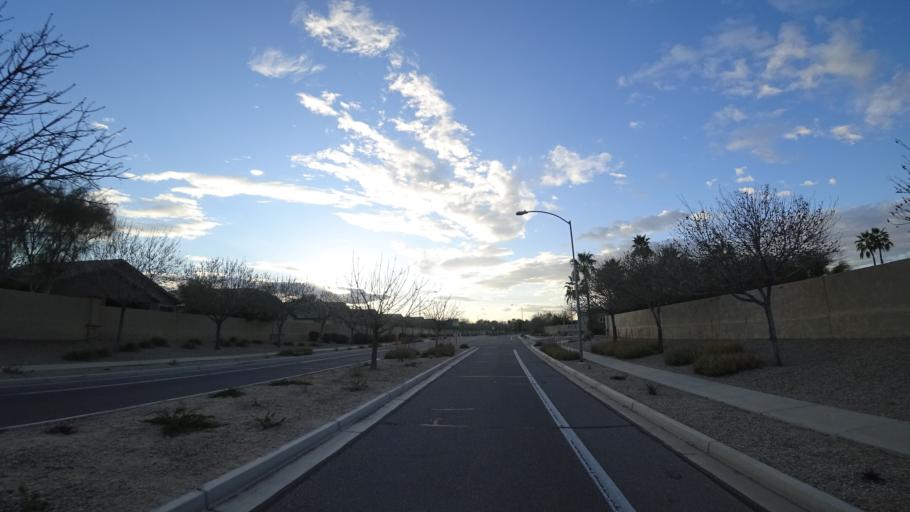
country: US
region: Arizona
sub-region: Maricopa County
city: Peoria
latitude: 33.5417
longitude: -112.2386
